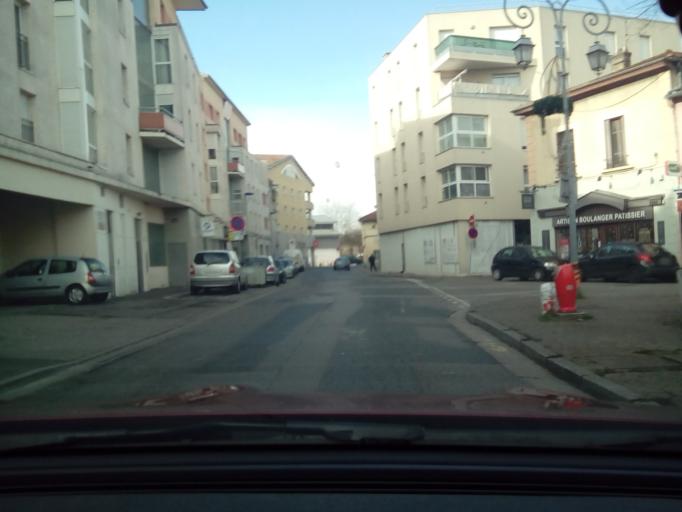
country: FR
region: Rhone-Alpes
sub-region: Departement du Rhone
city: Vaulx-en-Velin
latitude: 45.7857
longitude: 4.9286
